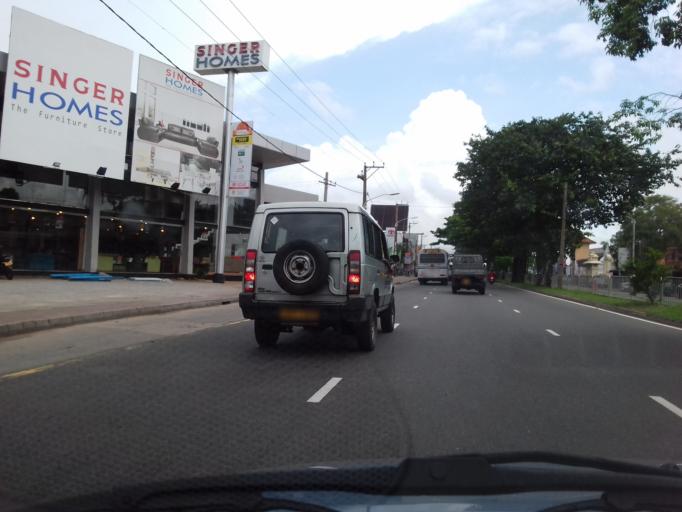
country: LK
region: Western
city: Galkissa
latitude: 6.8158
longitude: 79.8775
